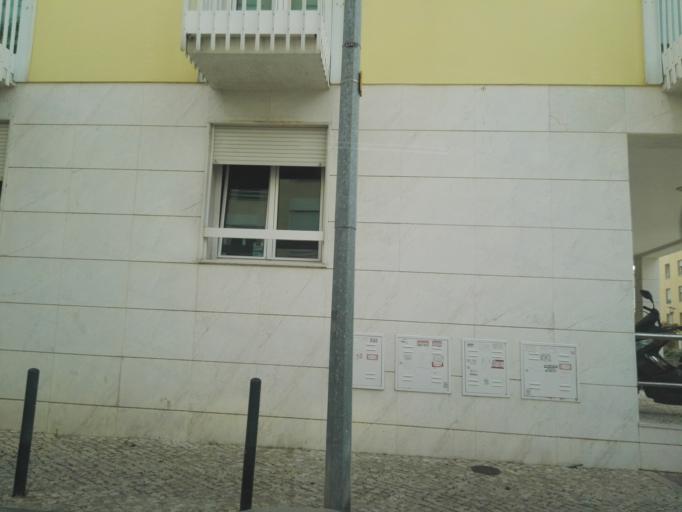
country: PT
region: Lisbon
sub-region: Loures
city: Moscavide
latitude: 38.7589
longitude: -9.0951
